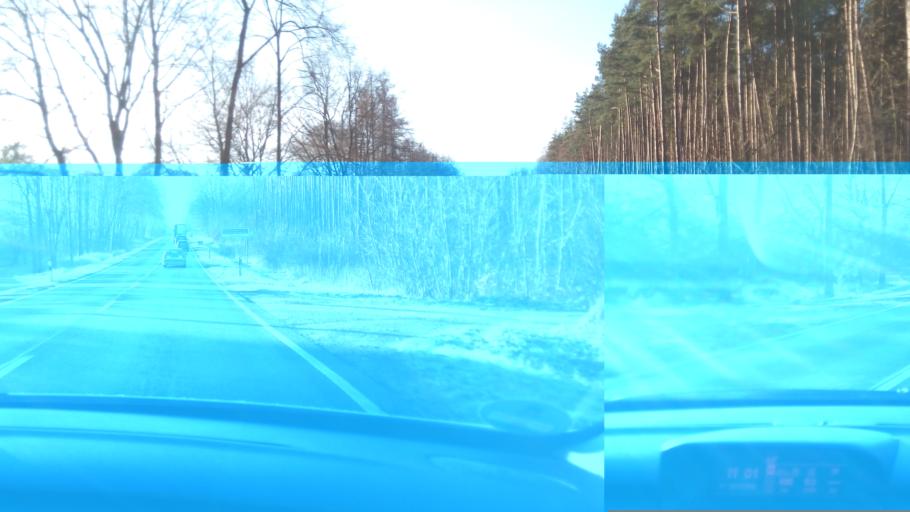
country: DE
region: Mecklenburg-Vorpommern
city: Neustrelitz
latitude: 53.3812
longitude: 13.0836
